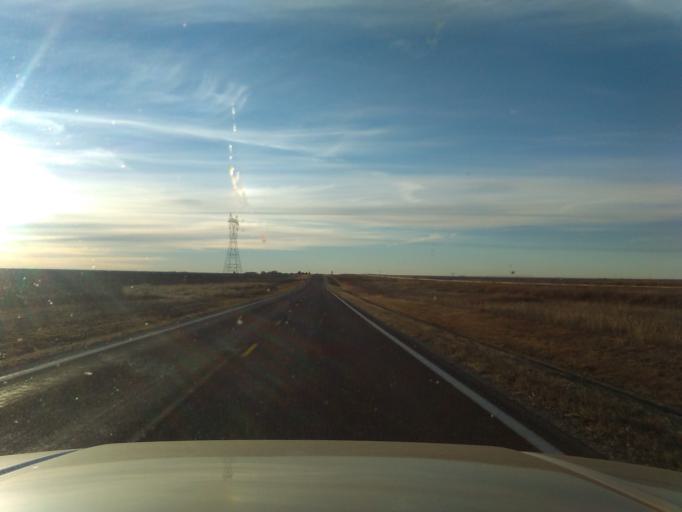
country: US
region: Kansas
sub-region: Logan County
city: Oakley
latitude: 39.1158
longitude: -100.9295
